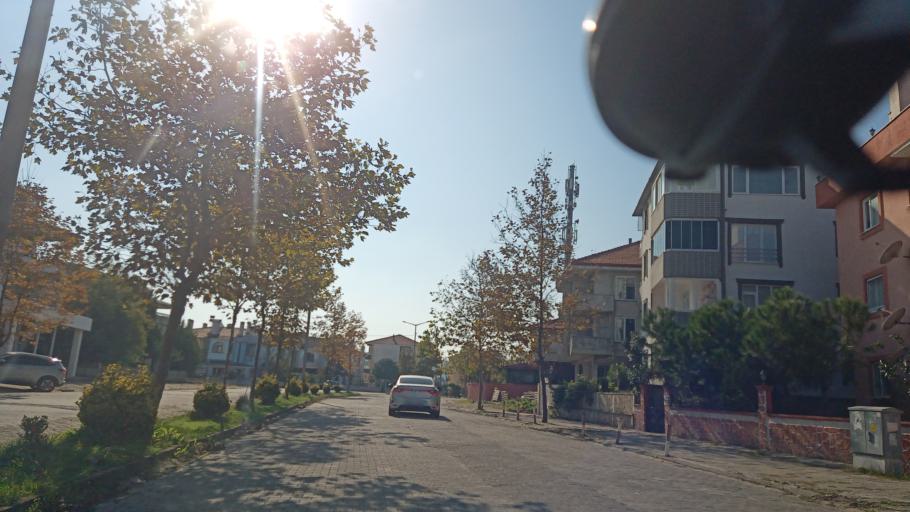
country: TR
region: Sakarya
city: Karasu
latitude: 41.0905
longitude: 30.7420
